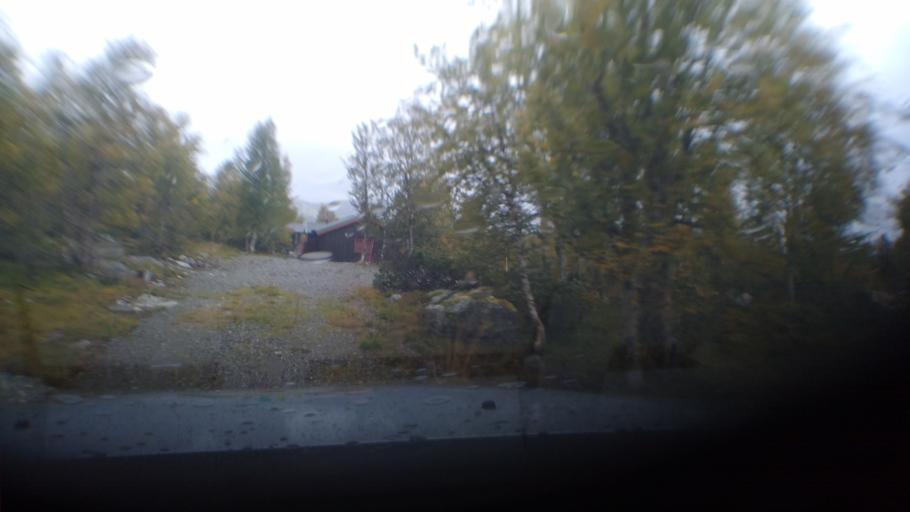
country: NO
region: Oppland
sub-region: Ringebu
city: Ringebu
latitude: 61.6628
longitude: 10.1013
